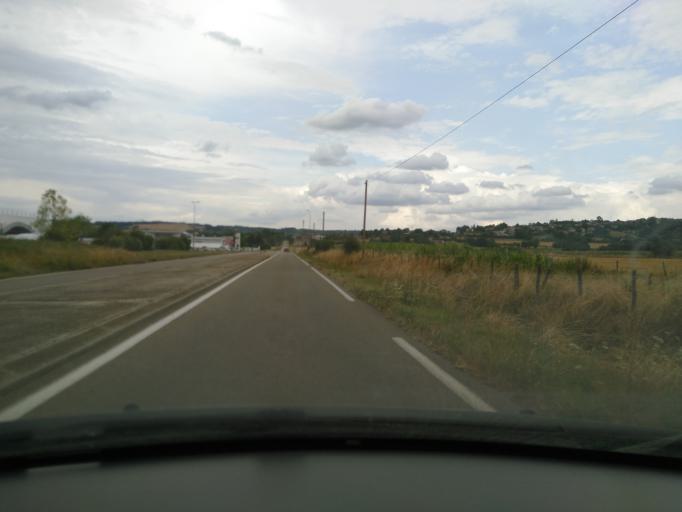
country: FR
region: Rhone-Alpes
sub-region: Departement de l'Isere
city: Beaurepaire
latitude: 45.3712
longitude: 5.0272
